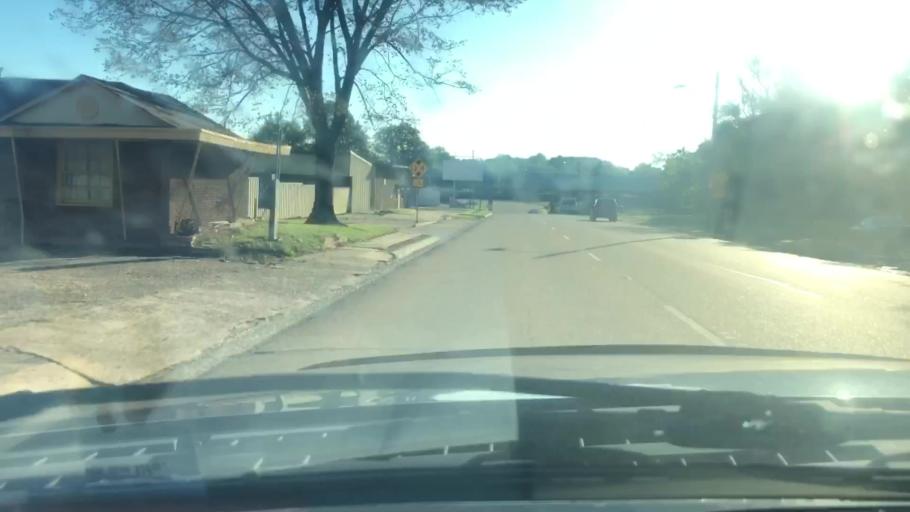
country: US
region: Texas
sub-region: Bowie County
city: Texarkana
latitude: 33.4233
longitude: -94.0549
